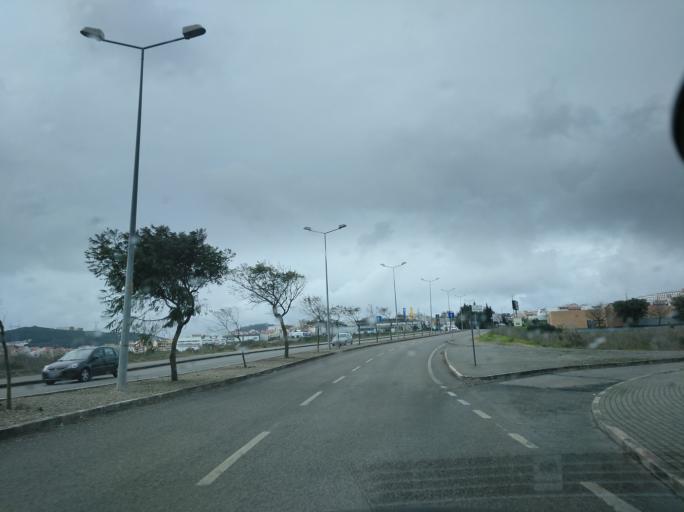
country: PT
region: Lisbon
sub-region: Odivelas
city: Famoes
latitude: 38.7898
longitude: -9.2122
